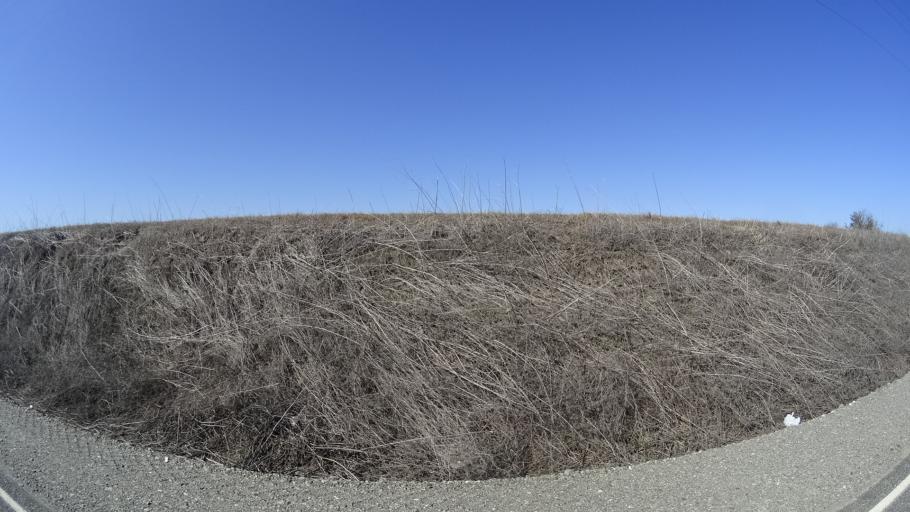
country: US
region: California
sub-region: Glenn County
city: Hamilton City
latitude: 39.7512
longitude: -122.0227
